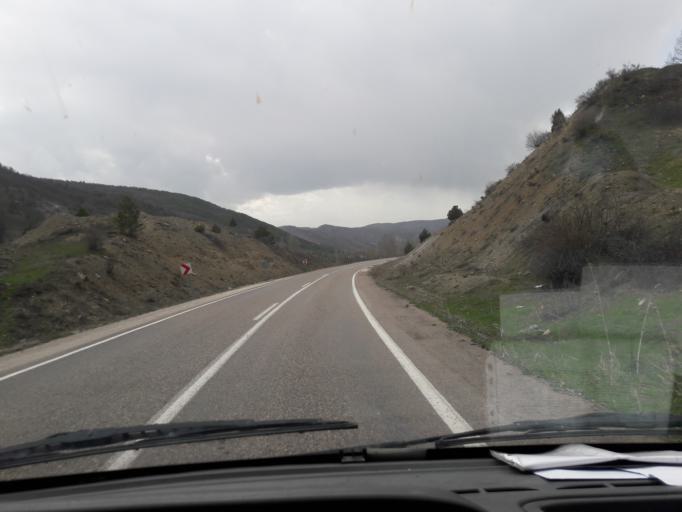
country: TR
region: Giresun
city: Alucra
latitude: 40.2730
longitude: 38.8615
